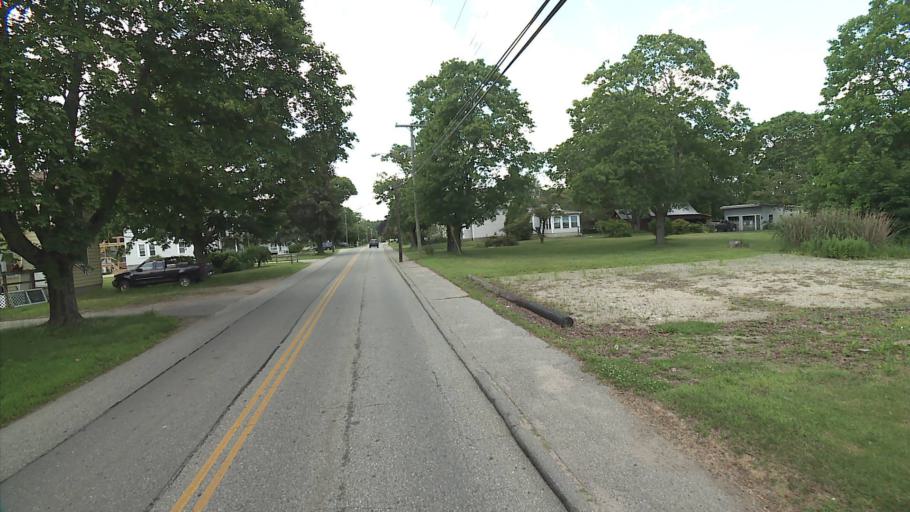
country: US
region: Connecticut
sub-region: New London County
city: Poquonock Bridge
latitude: 41.3435
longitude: -72.0390
